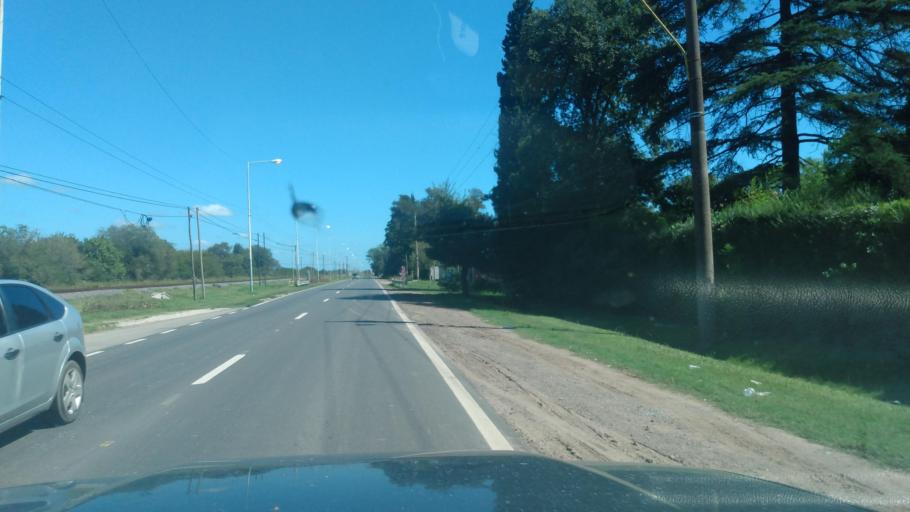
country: AR
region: Buenos Aires
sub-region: Partido de General Rodriguez
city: General Rodriguez
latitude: -34.5943
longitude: -59.0142
